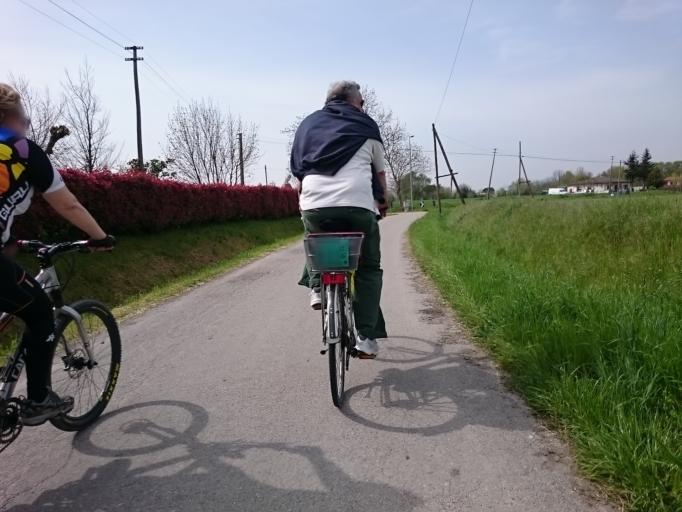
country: IT
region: Veneto
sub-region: Provincia di Padova
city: Tribano
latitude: 45.1909
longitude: 11.8301
